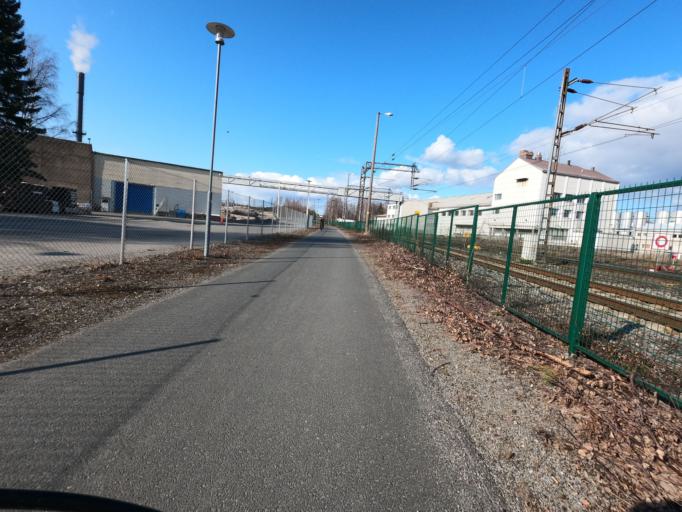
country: FI
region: North Karelia
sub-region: Joensuu
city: Joensuu
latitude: 62.6033
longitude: 29.7800
